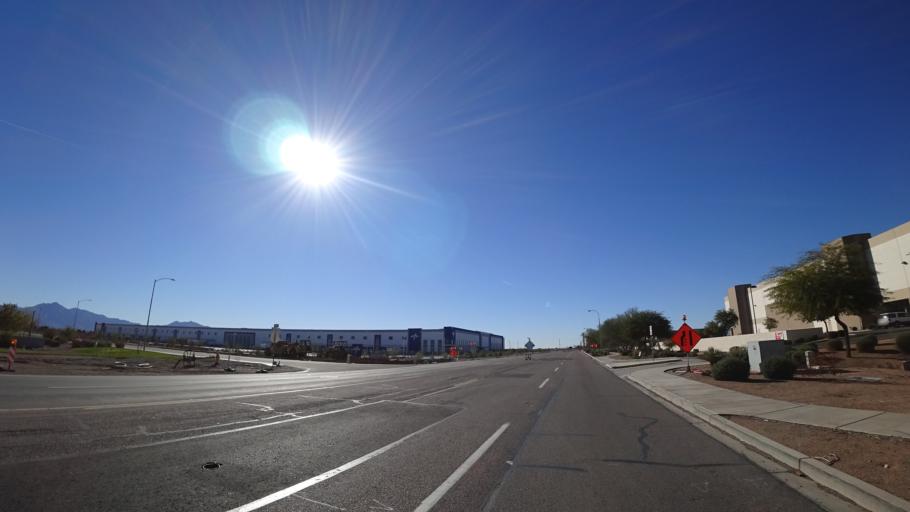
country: US
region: Arizona
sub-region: Maricopa County
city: Tolleson
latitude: 33.4366
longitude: -112.2460
